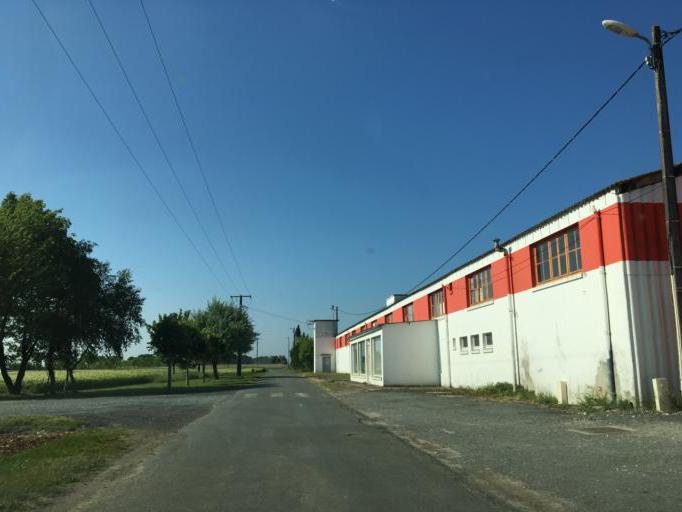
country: FR
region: Poitou-Charentes
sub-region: Departement des Deux-Sevres
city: Beauvoir-sur-Niort
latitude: 46.0901
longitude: -0.5060
